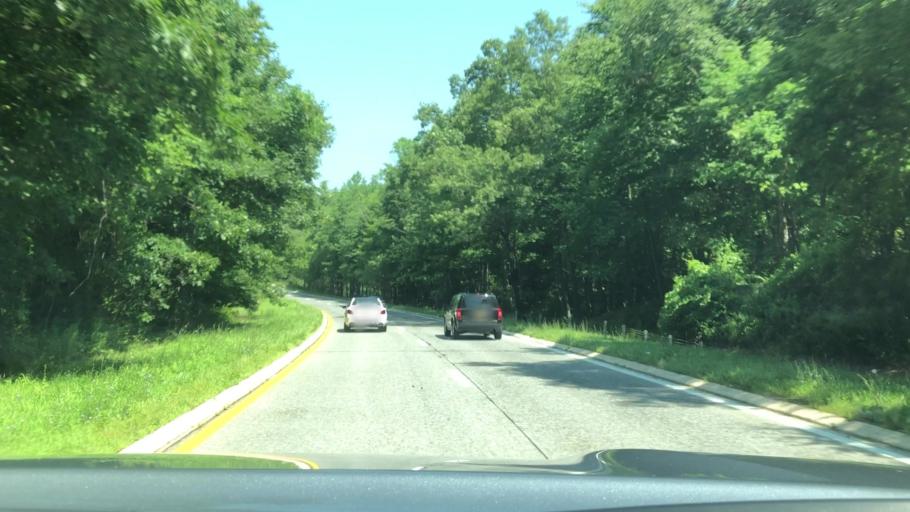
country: US
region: New York
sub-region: Rockland County
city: Stony Point
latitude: 41.2711
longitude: -74.0304
